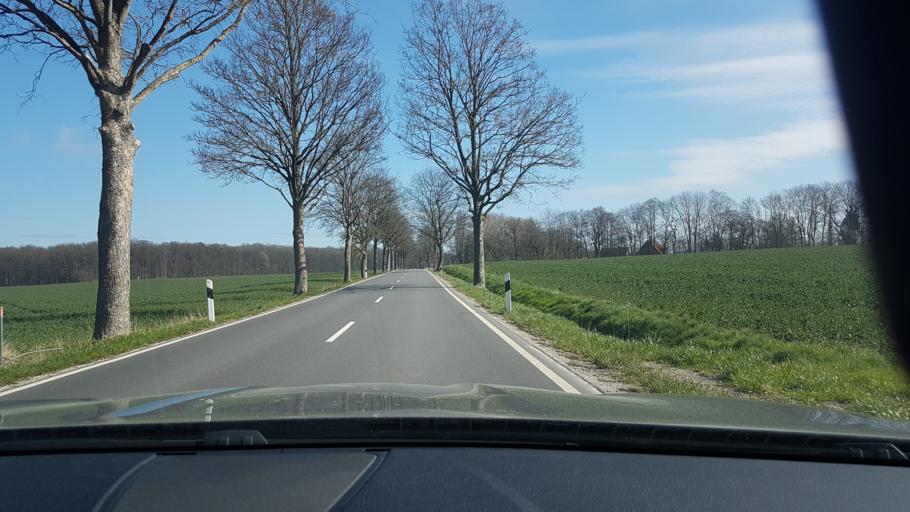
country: DE
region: Lower Saxony
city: Springe
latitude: 52.1628
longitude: 9.6099
